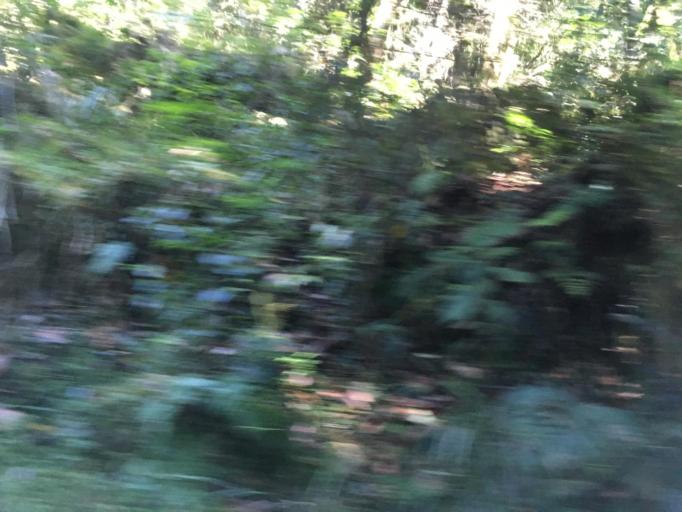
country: TW
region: Taiwan
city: Daxi
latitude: 24.5830
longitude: 121.4132
